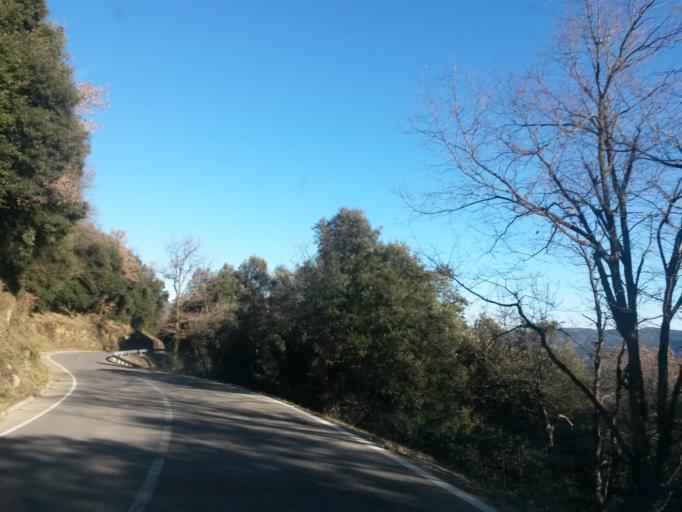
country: ES
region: Catalonia
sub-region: Provincia de Girona
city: Sant Feliu de Pallerols
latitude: 42.0755
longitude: 2.4839
